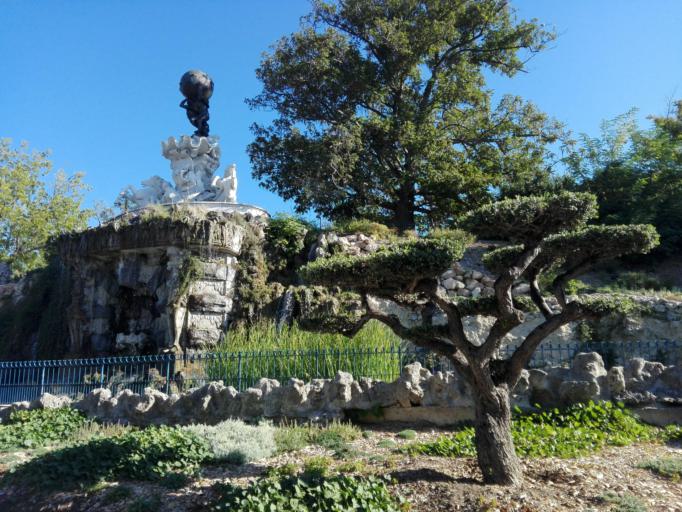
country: FR
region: Languedoc-Roussillon
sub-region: Departement de l'Herault
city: Beziers
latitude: 43.3381
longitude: 3.2202
